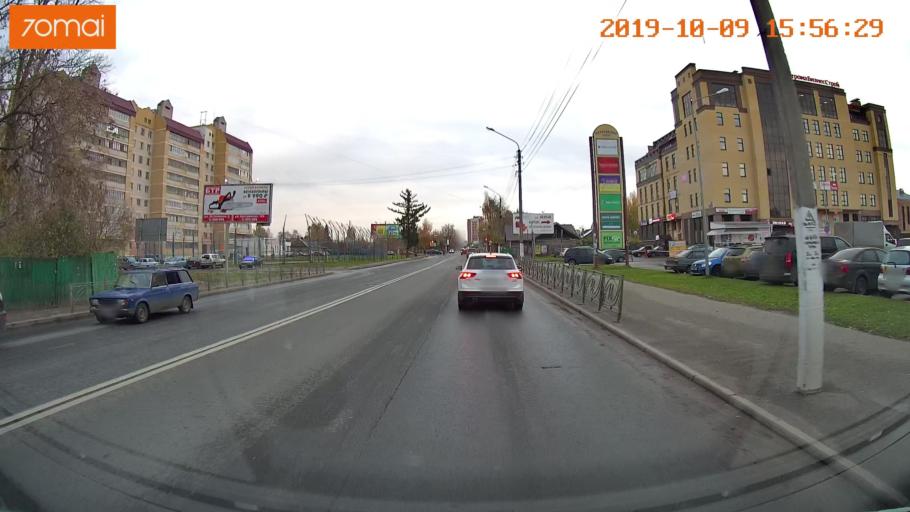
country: RU
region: Kostroma
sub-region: Kostromskoy Rayon
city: Kostroma
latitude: 57.7746
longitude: 40.9457
